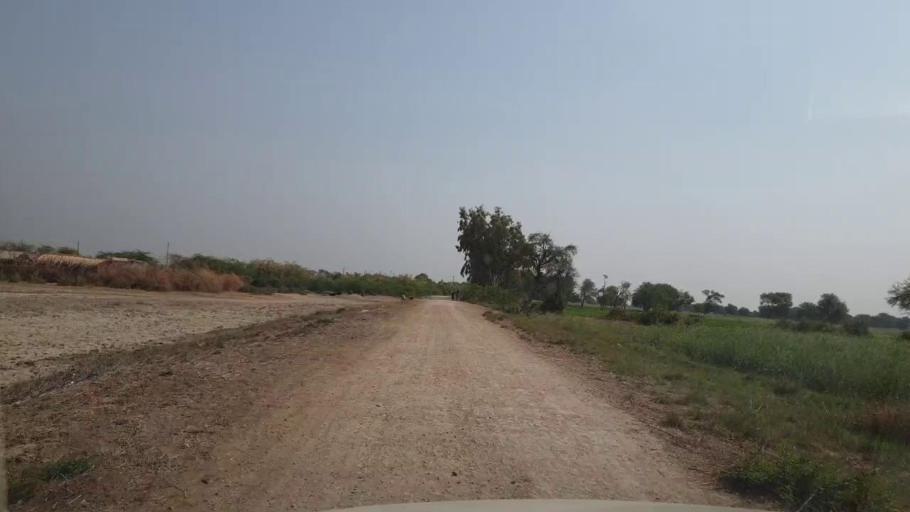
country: PK
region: Sindh
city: Dhoro Naro
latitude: 25.4576
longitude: 69.6294
